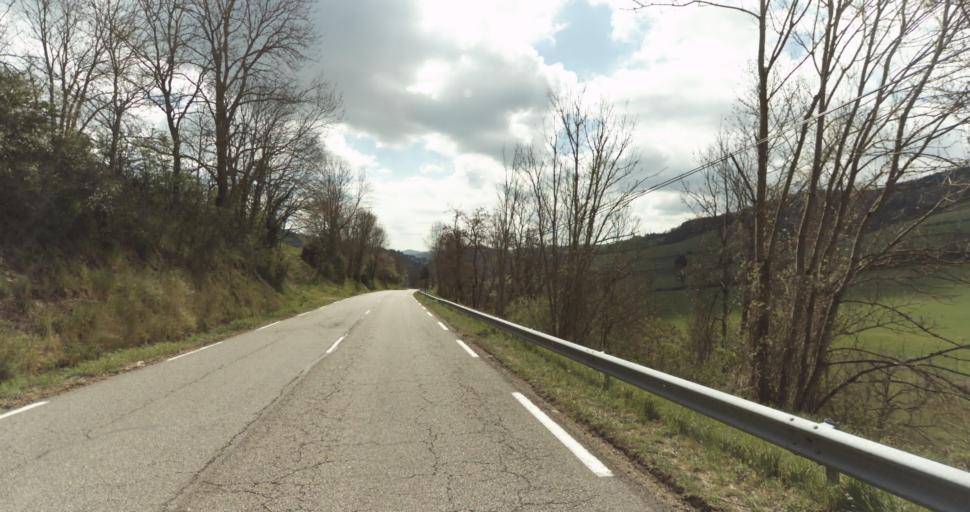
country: FR
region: Rhone-Alpes
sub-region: Departement du Rhone
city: Tarare
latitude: 45.9162
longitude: 4.4182
